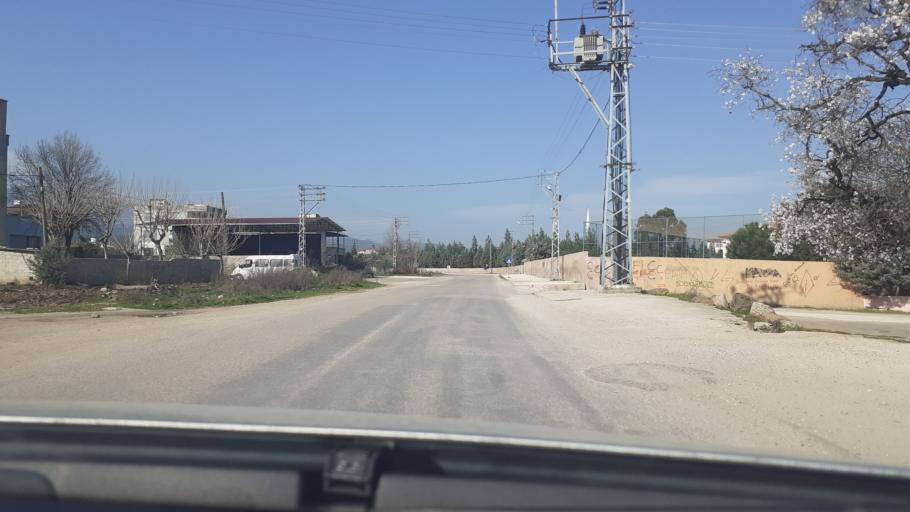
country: TR
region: Hatay
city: Aktepe
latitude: 36.7068
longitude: 36.4870
